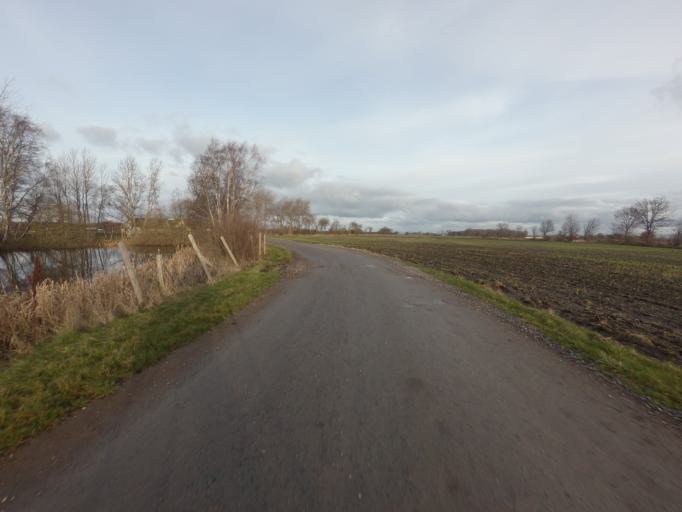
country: SE
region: Skane
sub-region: Hoganas Kommun
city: Hoganas
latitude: 56.1730
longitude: 12.5828
